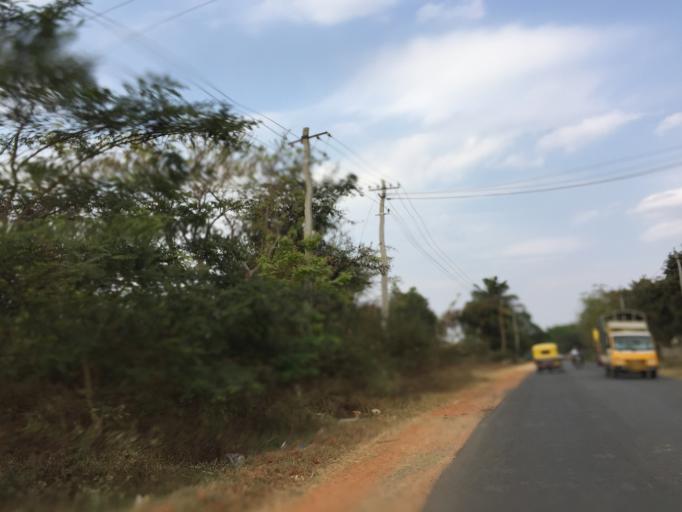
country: IN
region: Karnataka
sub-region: Chikkaballapur
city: Chik Ballapur
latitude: 13.4127
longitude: 77.7168
